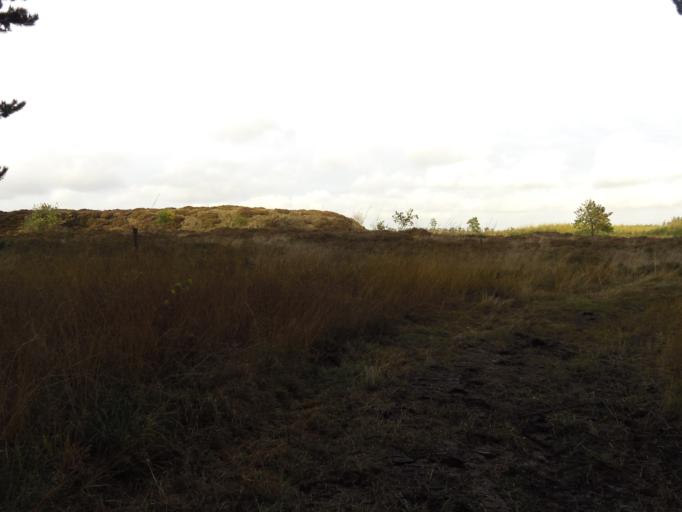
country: DK
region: South Denmark
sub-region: Haderslev Kommune
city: Gram
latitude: 55.2694
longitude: 8.9665
